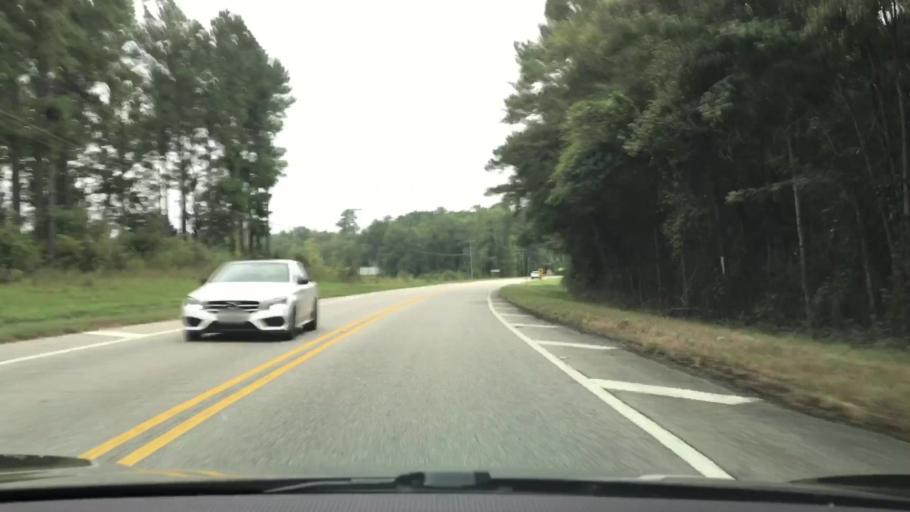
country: US
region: Alabama
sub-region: Coffee County
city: Elba
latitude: 31.4591
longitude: -86.0691
